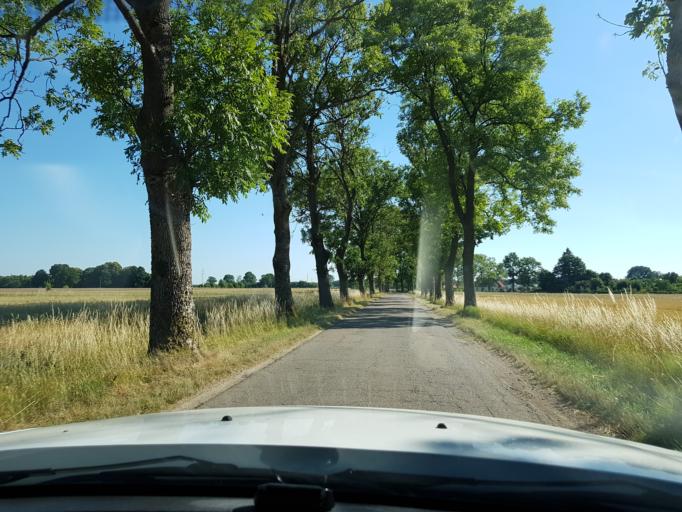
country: PL
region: West Pomeranian Voivodeship
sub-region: Powiat swidwinski
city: Slawoborze
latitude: 53.8228
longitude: 15.6876
